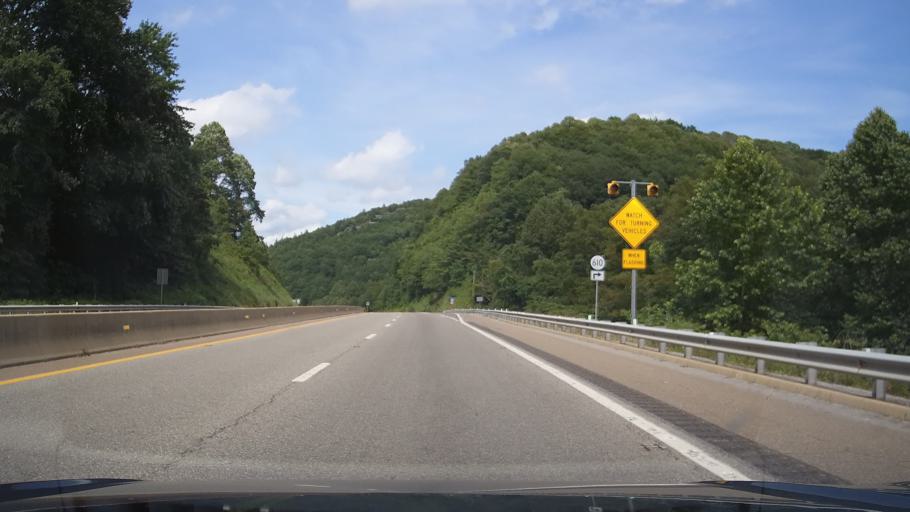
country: US
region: Virginia
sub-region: City of Norton
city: Norton
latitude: 36.9151
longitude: -82.6669
